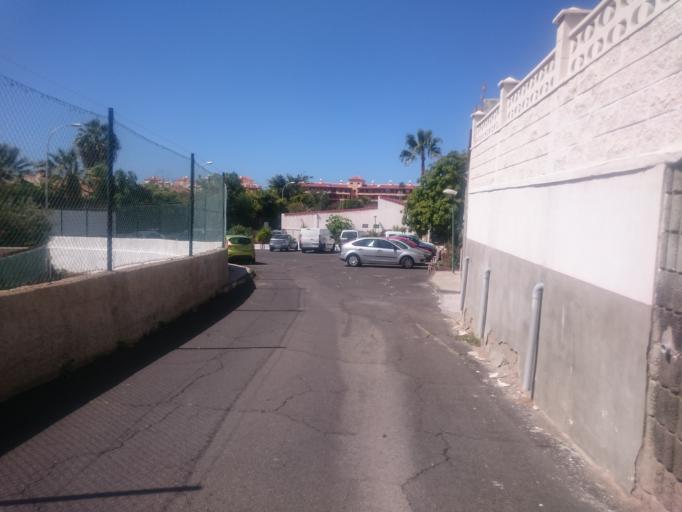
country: ES
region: Canary Islands
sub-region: Provincia de Santa Cruz de Tenerife
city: Playa de las Americas
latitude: 28.0560
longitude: -16.7055
